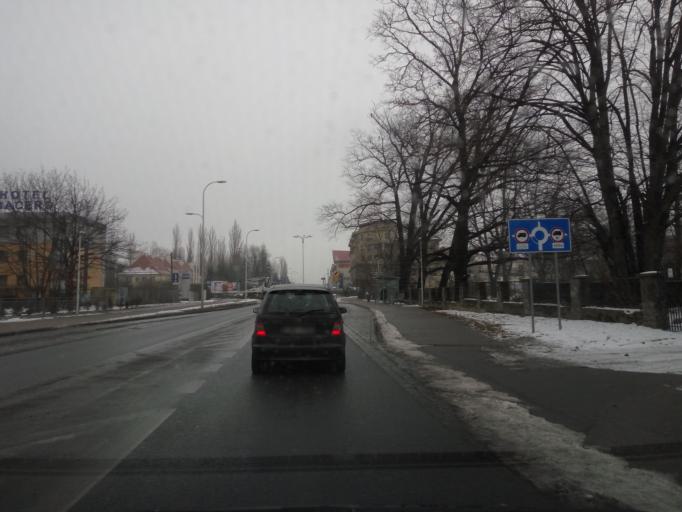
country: PL
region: Lower Silesian Voivodeship
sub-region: Powiat wroclawski
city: Bielany Wroclawskie
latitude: 51.0596
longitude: 17.0055
